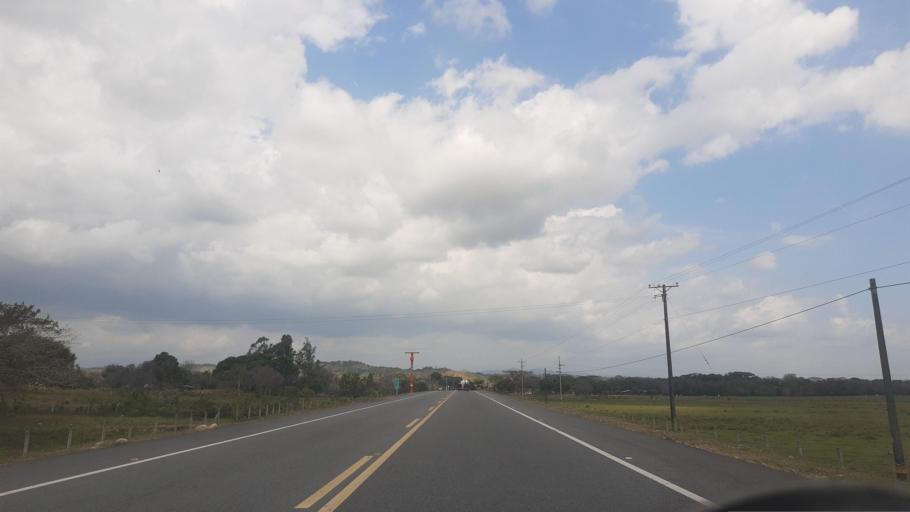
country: CO
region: Casanare
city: Tauramena
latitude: 4.9119
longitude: -72.6757
